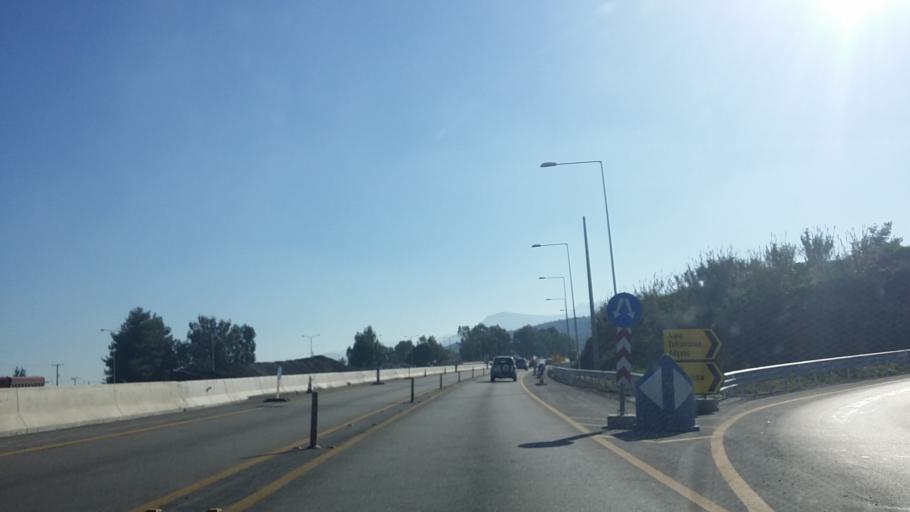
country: GR
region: West Greece
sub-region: Nomos Achaias
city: Selianitika
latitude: 38.2865
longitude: 22.0210
